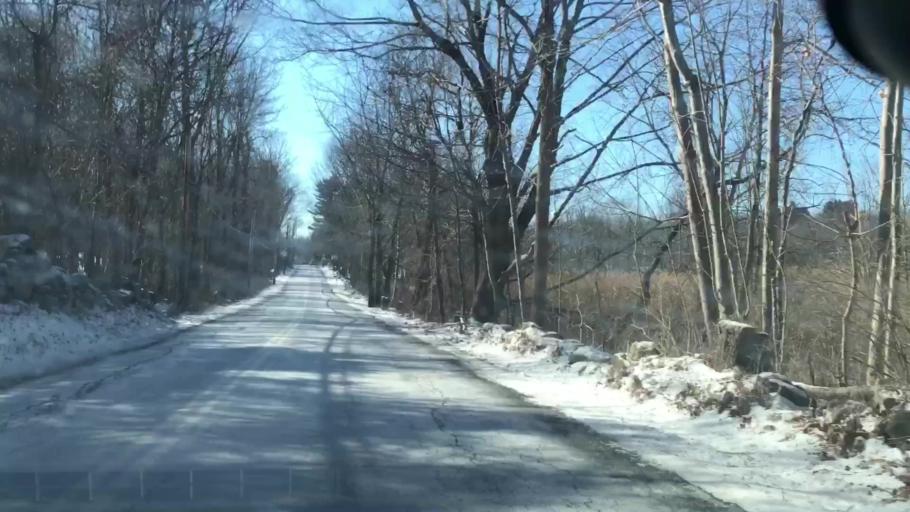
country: US
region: New York
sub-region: Putnam County
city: Mahopac
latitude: 41.3820
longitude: -73.7069
